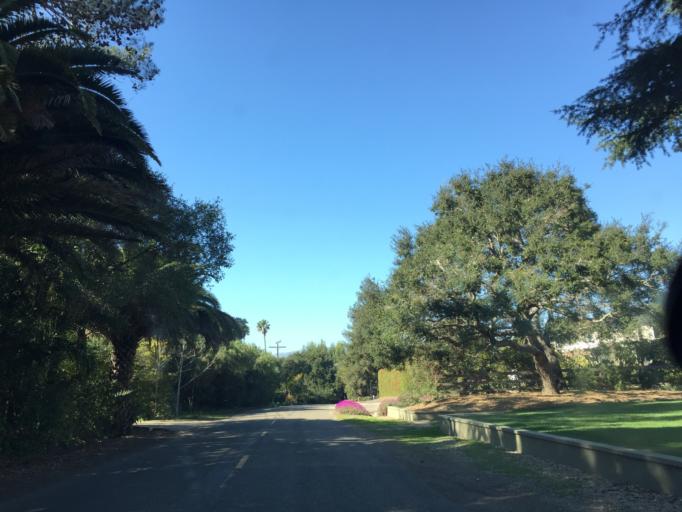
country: US
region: California
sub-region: Santa Barbara County
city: Mission Canyon
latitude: 34.4350
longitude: -119.7602
